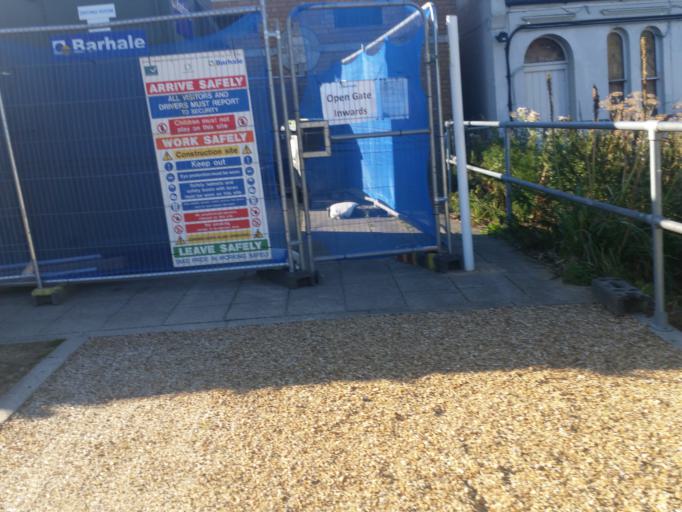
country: GB
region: England
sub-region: Greater London
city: Wood Green
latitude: 51.5895
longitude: -0.1146
